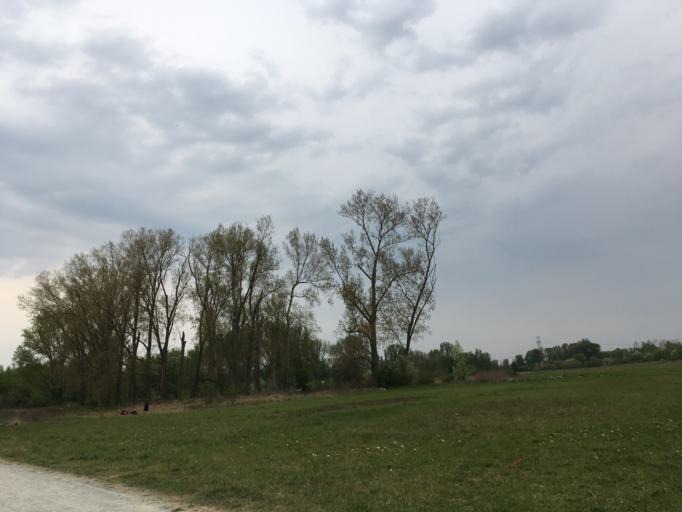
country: DE
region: Berlin
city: Wartenberg
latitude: 52.5813
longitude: 13.5009
